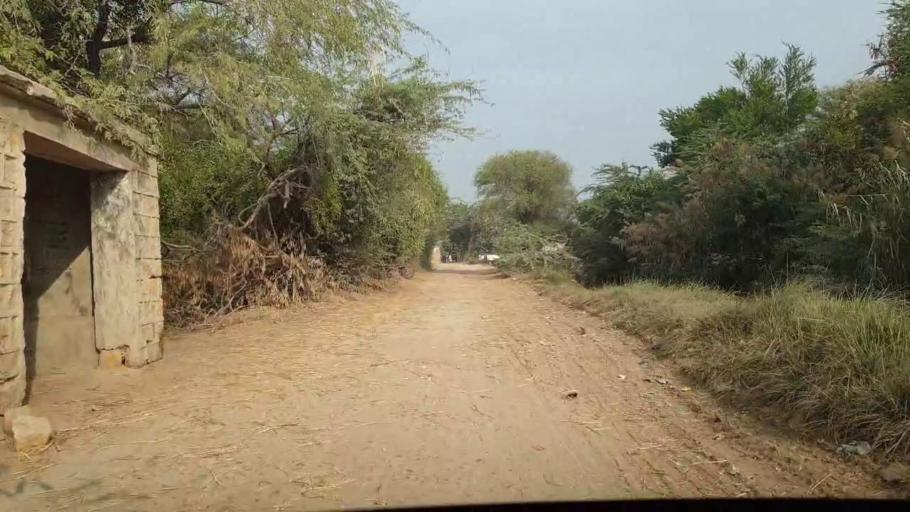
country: PK
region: Sindh
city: Chuhar Jamali
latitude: 24.3964
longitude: 67.9730
